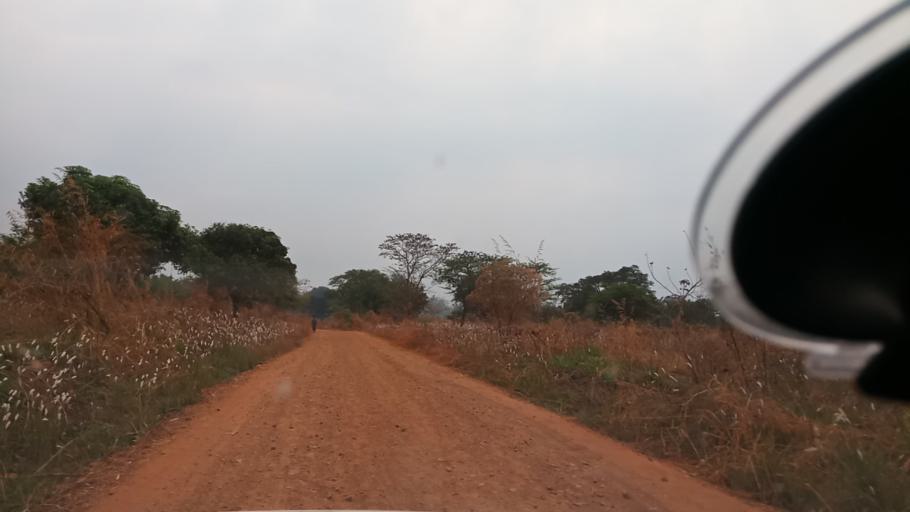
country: ZM
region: Luapula
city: Nchelenge
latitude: -9.0933
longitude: 28.3276
